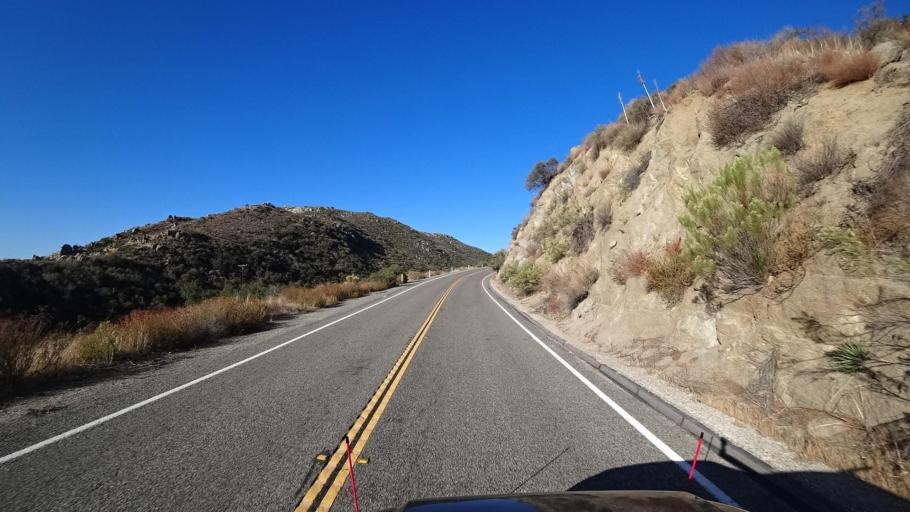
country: MX
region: Baja California
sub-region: Tecate
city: Hacienda Tecate
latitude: 32.5988
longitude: -116.5682
